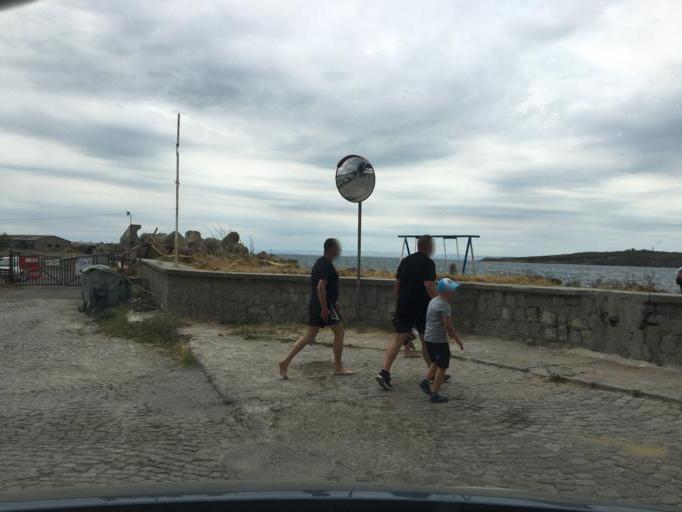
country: BG
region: Burgas
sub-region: Obshtina Sozopol
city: Sozopol
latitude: 42.4256
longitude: 27.6947
